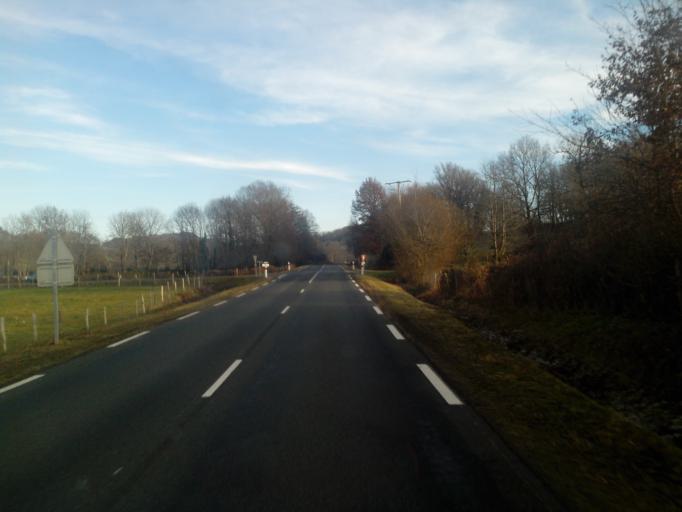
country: FR
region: Limousin
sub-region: Departement de la Correze
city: Bort-les-Orgues
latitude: 45.3559
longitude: 2.5146
